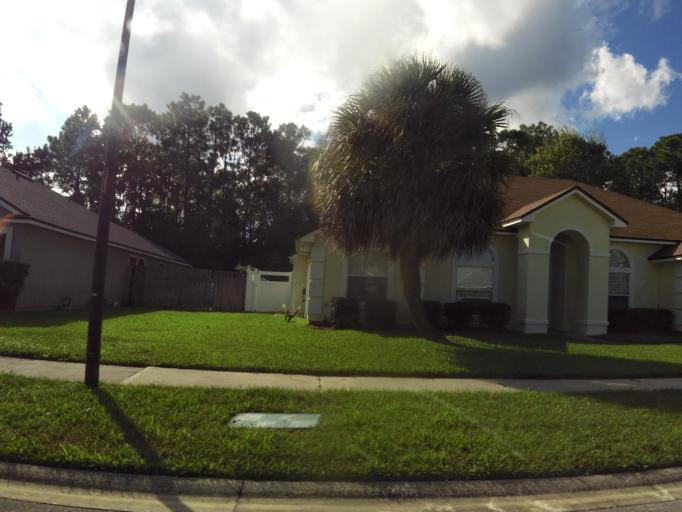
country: US
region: Florida
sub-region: Duval County
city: Jacksonville Beach
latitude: 30.2745
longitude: -81.4967
